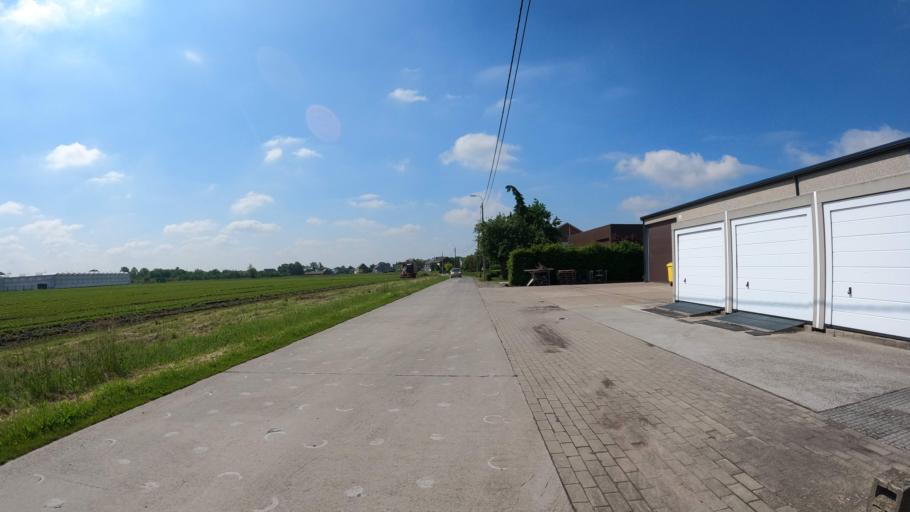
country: BE
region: Flanders
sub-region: Provincie Antwerpen
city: Sint-Katelijne-Waver
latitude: 51.0794
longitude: 4.5204
